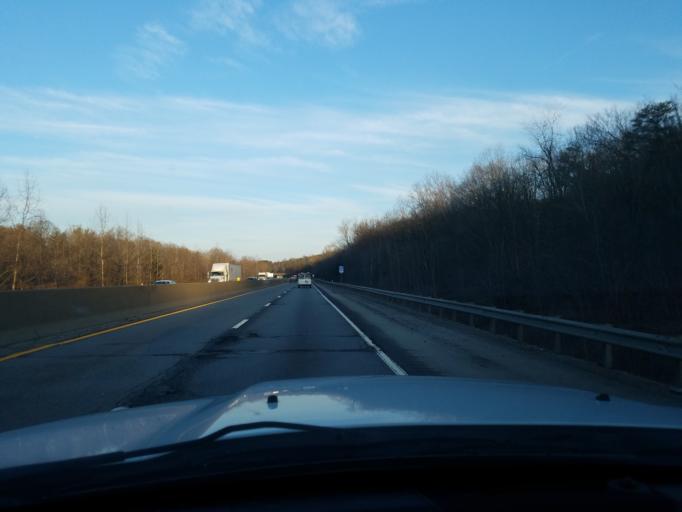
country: US
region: West Virginia
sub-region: Kanawha County
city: Nitro
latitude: 38.4506
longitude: -81.8546
